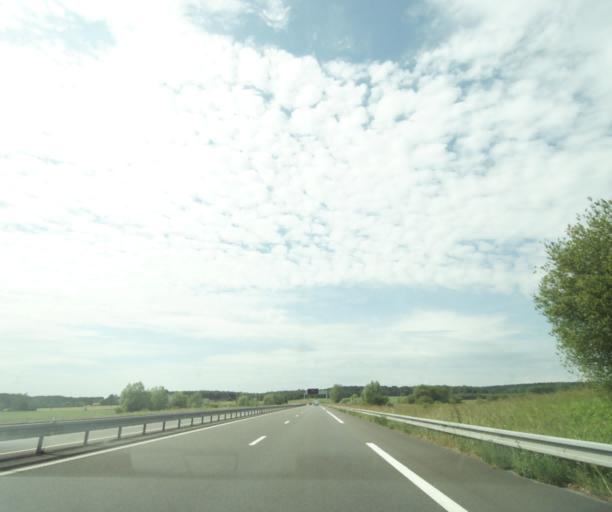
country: FR
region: Pays de la Loire
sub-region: Departement de Maine-et-Loire
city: Baune
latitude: 47.5284
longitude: -0.3145
